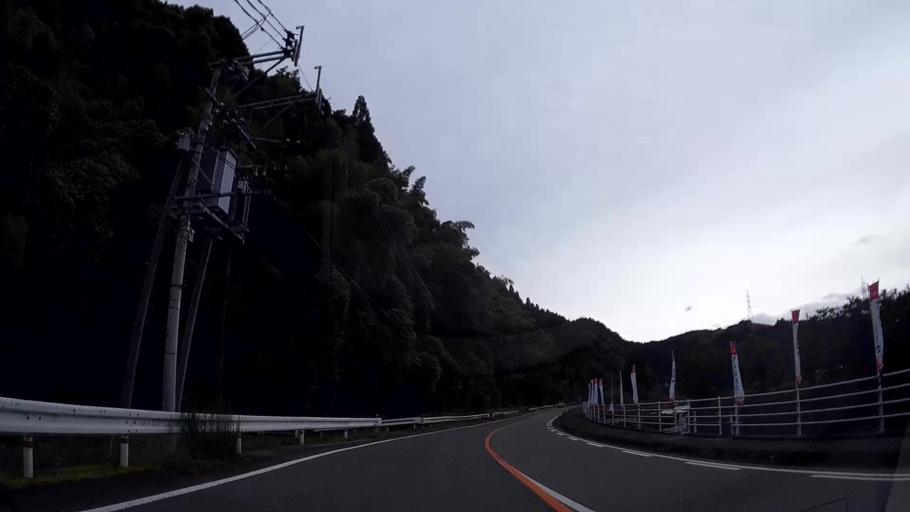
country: JP
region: Kumamoto
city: Kikuchi
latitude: 33.0145
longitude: 130.8873
